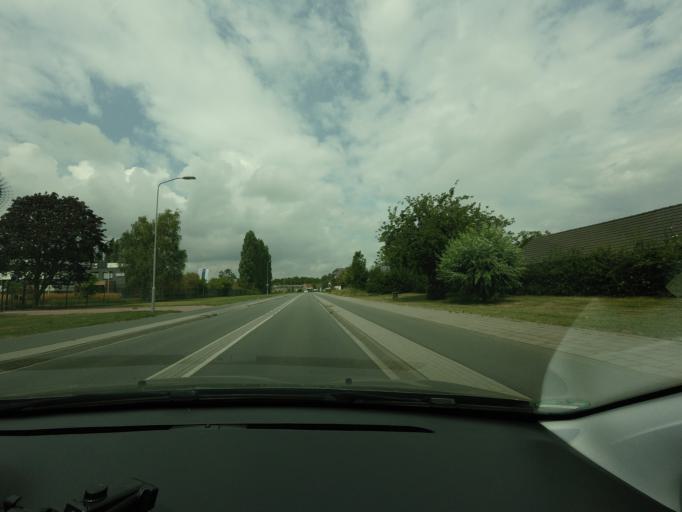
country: NL
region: Gelderland
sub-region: Gemeente Tiel
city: Tiel
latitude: 51.8838
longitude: 5.4197
